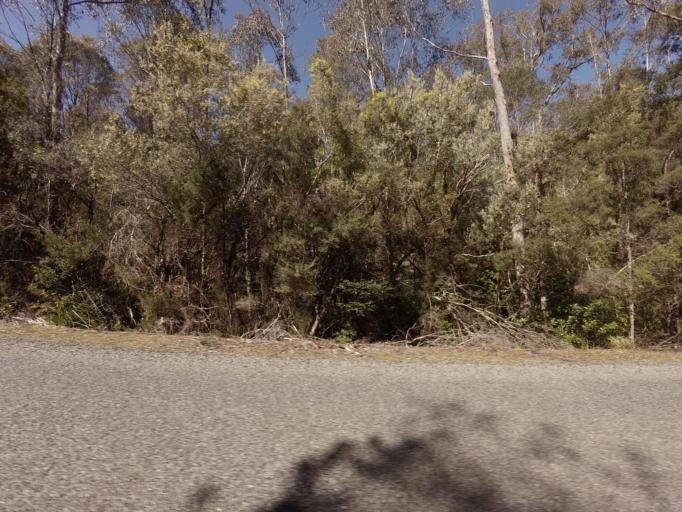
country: AU
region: Tasmania
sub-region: Derwent Valley
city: New Norfolk
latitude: -42.7645
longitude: 146.3972
